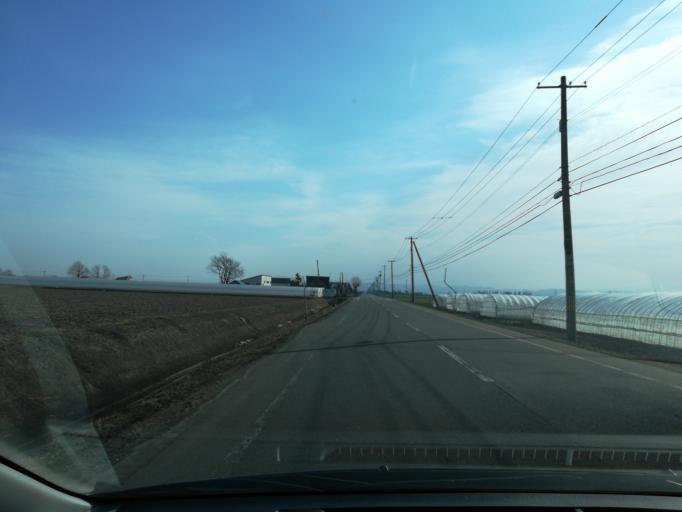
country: JP
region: Hokkaido
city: Iwamizawa
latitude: 43.1663
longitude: 141.6601
